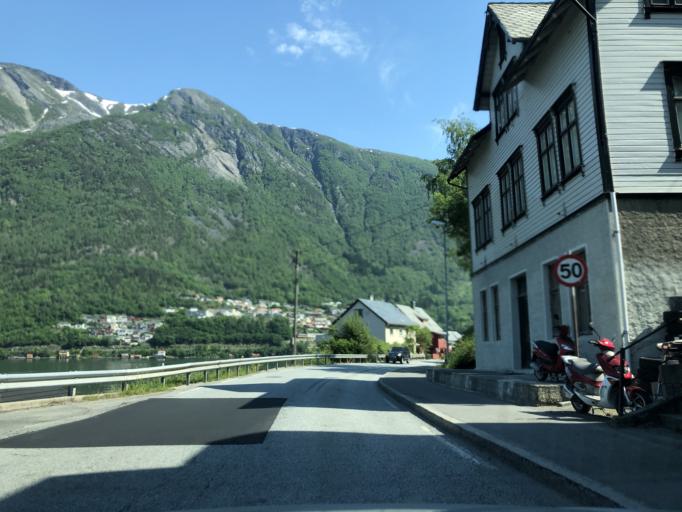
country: NO
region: Hordaland
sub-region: Odda
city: Odda
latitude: 60.0753
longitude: 6.5358
